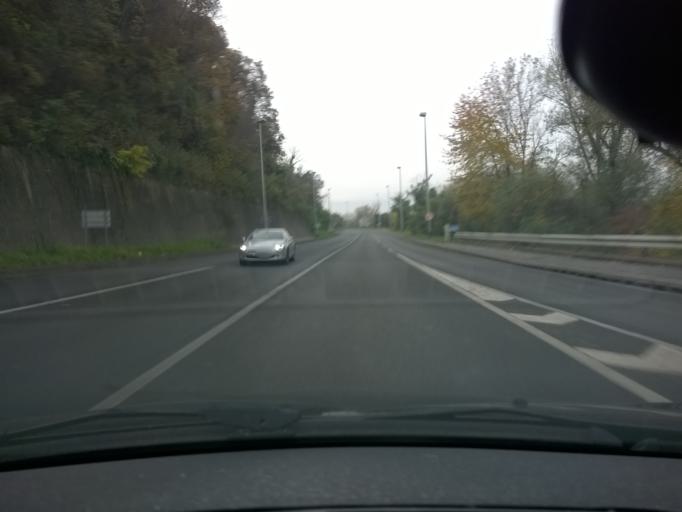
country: HR
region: Zagrebacka
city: Zapresic
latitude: 45.8356
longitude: 15.8240
